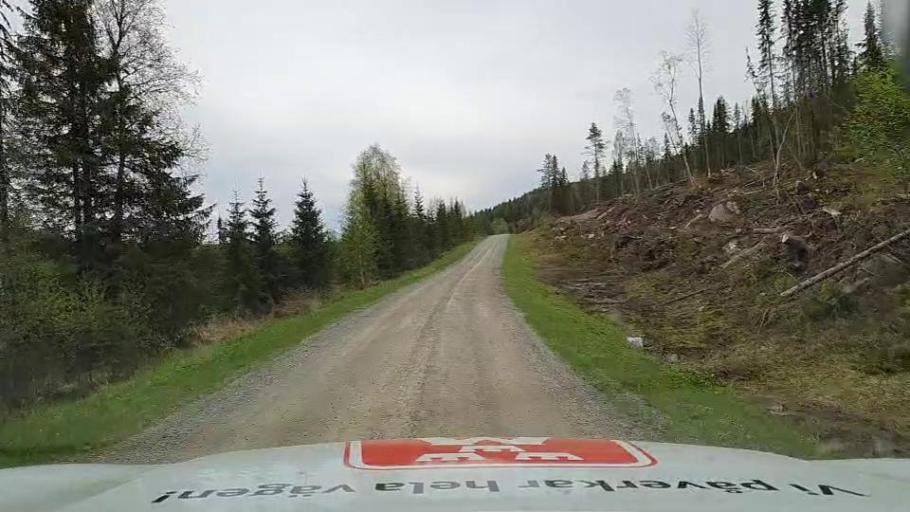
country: SE
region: Jaemtland
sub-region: Bergs Kommun
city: Hoverberg
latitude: 62.5545
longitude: 14.6909
